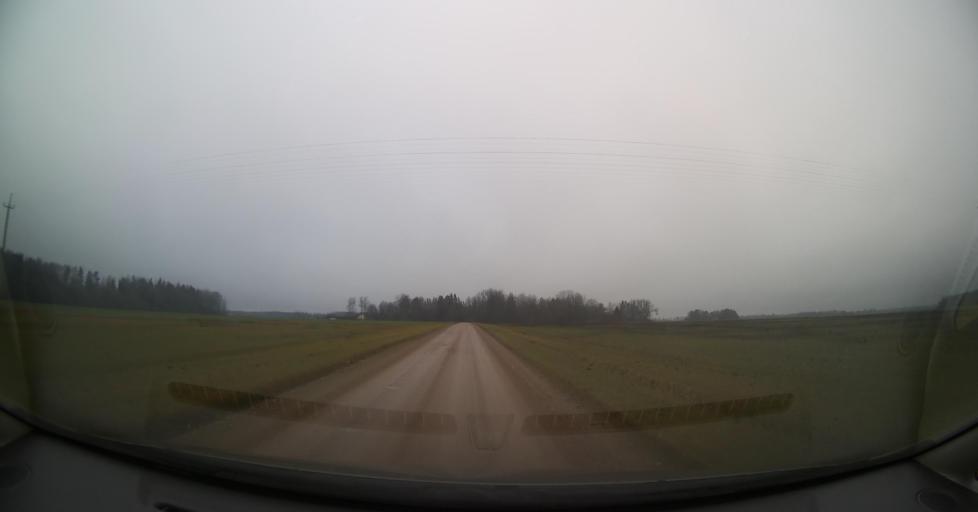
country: EE
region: Tartu
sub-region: Tartu linn
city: Tartu
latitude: 58.3755
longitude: 26.9303
